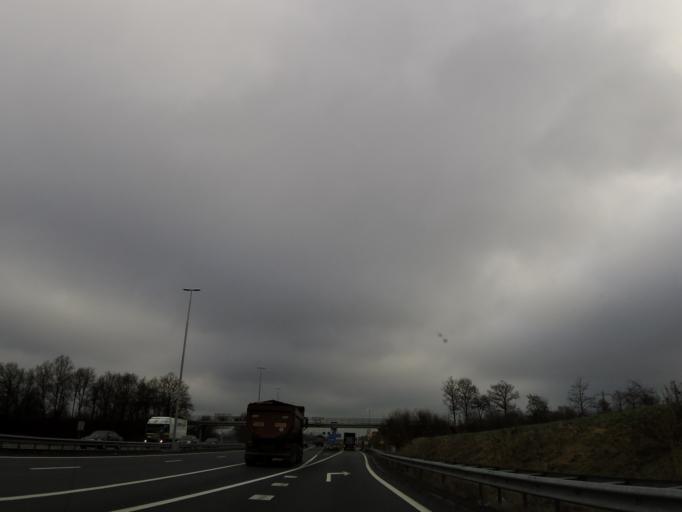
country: NL
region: Limburg
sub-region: Gemeente Maasgouw
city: Maasbracht
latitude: 51.1117
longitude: 5.8635
